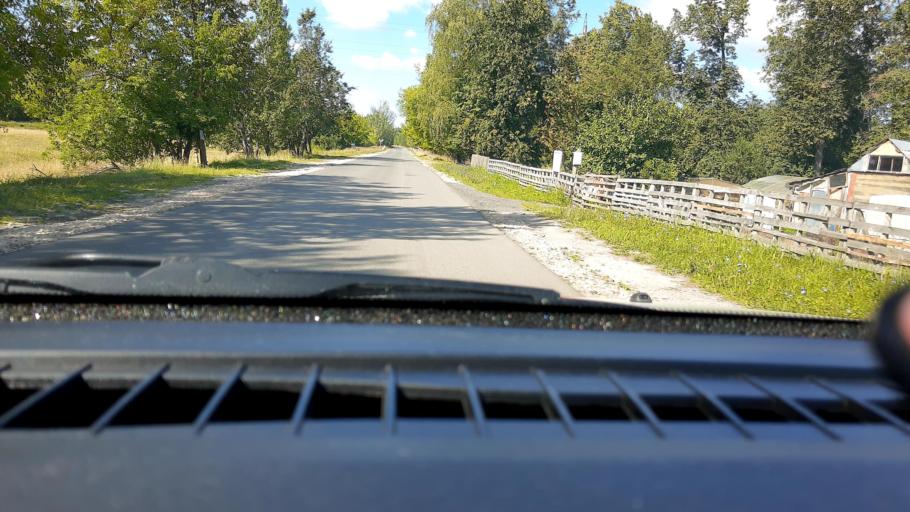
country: RU
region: Nizjnij Novgorod
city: Gorbatovka
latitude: 56.2642
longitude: 43.7261
